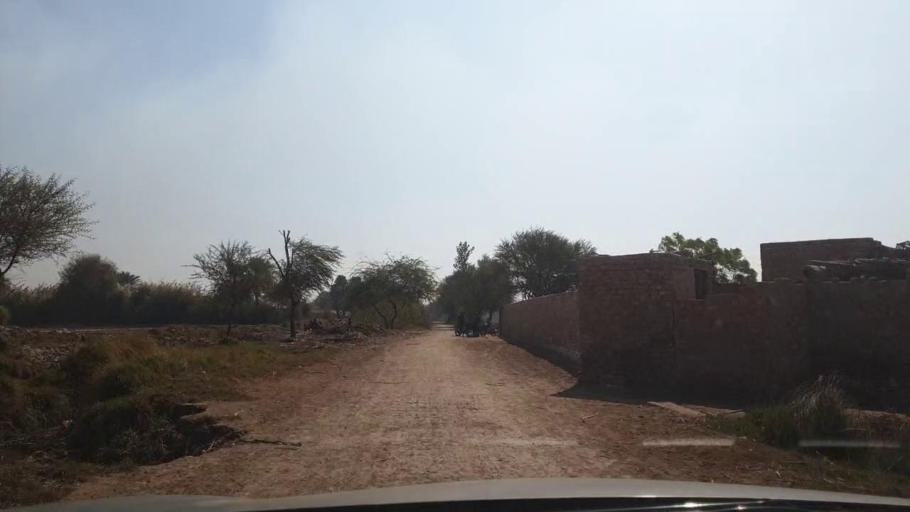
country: PK
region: Sindh
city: Tando Allahyar
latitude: 25.5912
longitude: 68.6552
